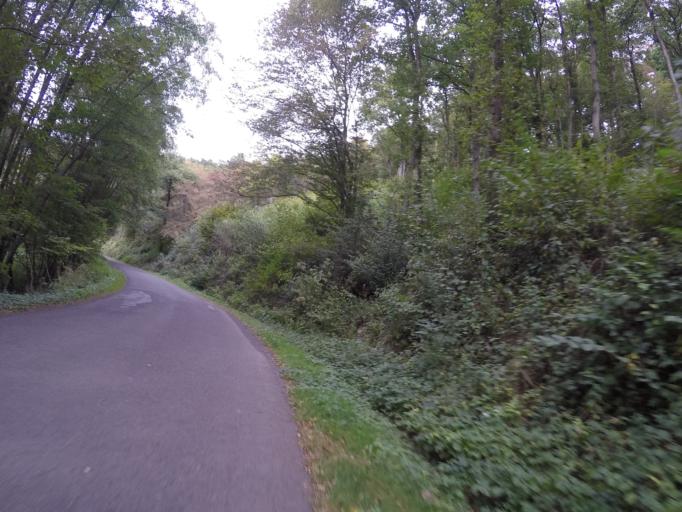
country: BE
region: Wallonia
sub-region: Province de Namur
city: Dinant
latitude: 50.2730
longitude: 4.9621
